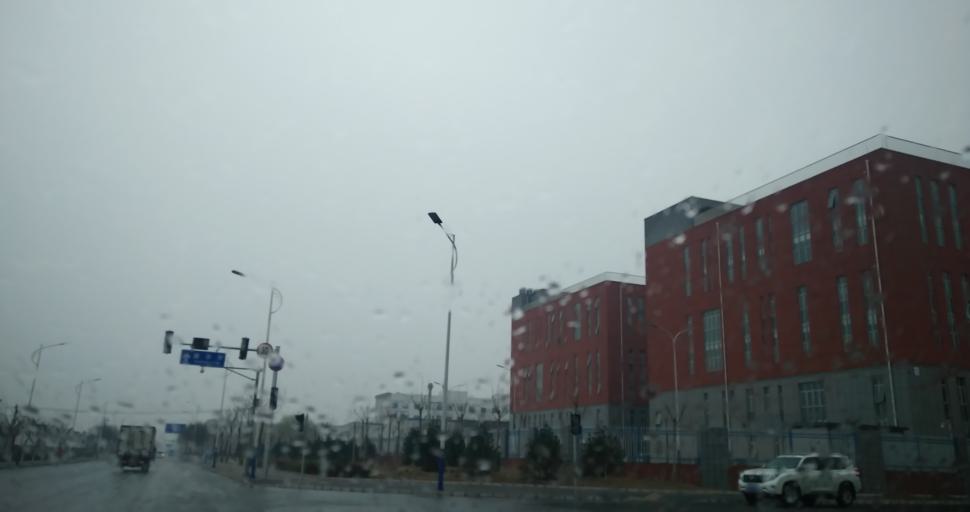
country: CN
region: Beijing
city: Yinghai
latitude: 39.7113
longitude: 116.4148
